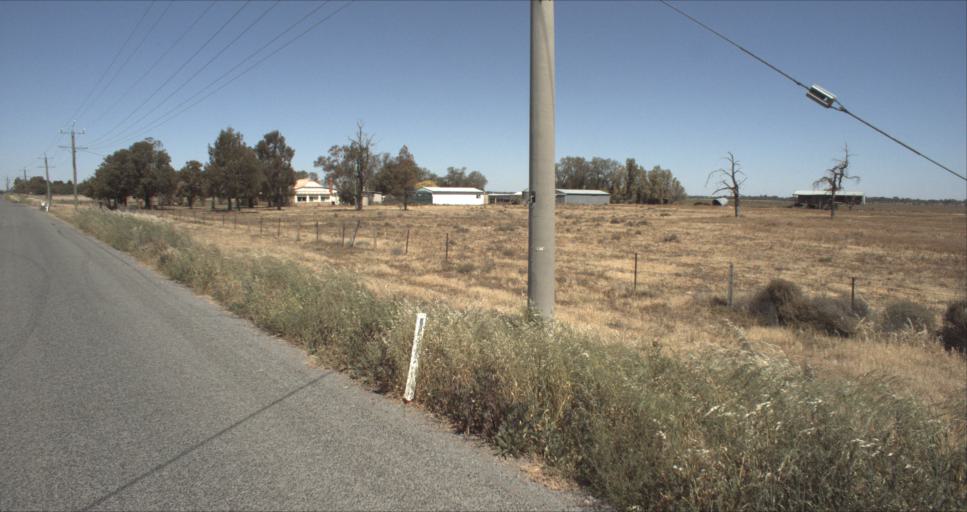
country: AU
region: New South Wales
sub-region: Leeton
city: Leeton
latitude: -34.5166
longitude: 146.4340
